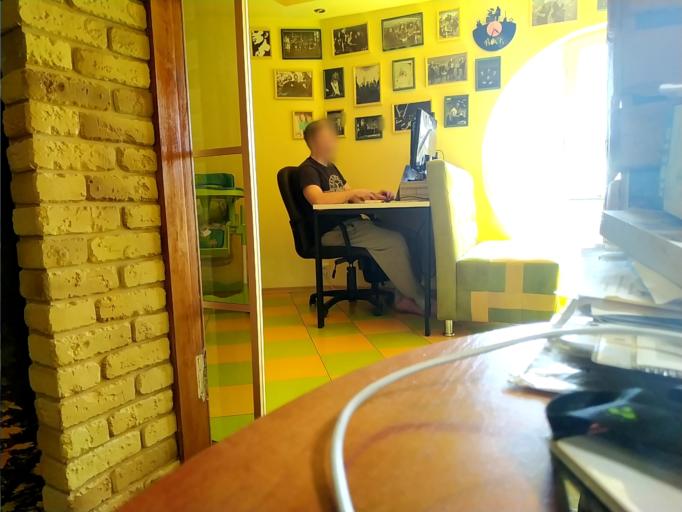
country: RU
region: Moskovskaya
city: Pavlovskiy Posad
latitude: 55.7450
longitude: 38.6875
